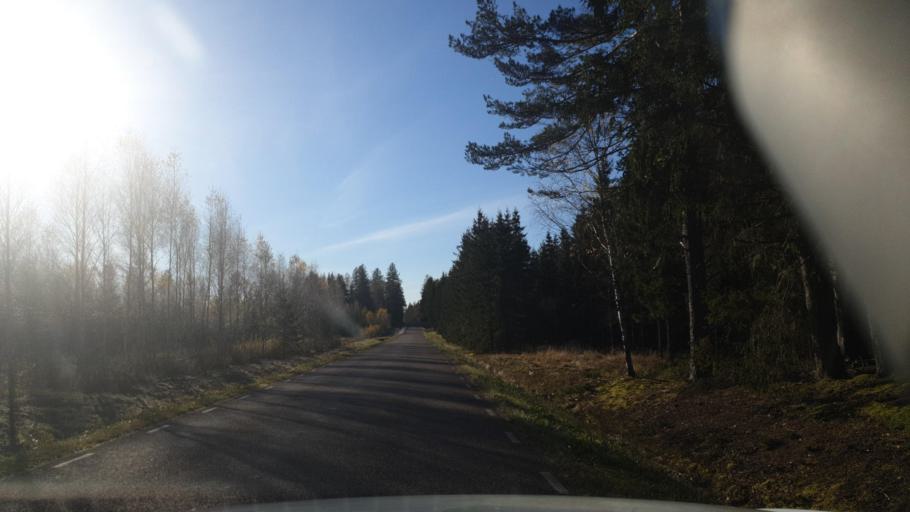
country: SE
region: Vaermland
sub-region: Karlstads Kommun
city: Edsvalla
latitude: 59.4646
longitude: 13.0835
